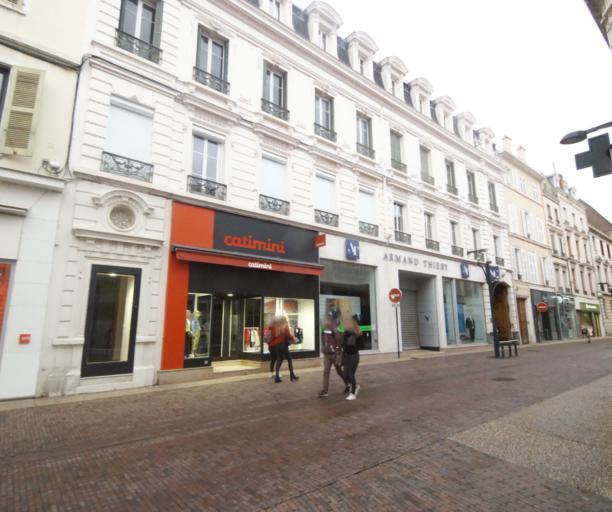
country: FR
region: Rhone-Alpes
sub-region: Departement de la Loire
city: Roanne
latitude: 46.0366
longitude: 4.0709
